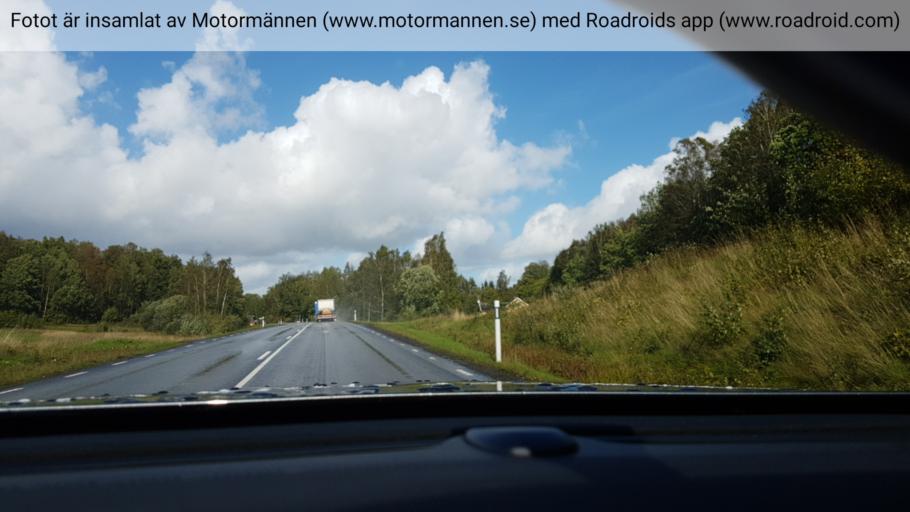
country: SE
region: Vaestra Goetaland
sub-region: Alingsas Kommun
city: Sollebrunn
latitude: 58.0465
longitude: 12.4679
